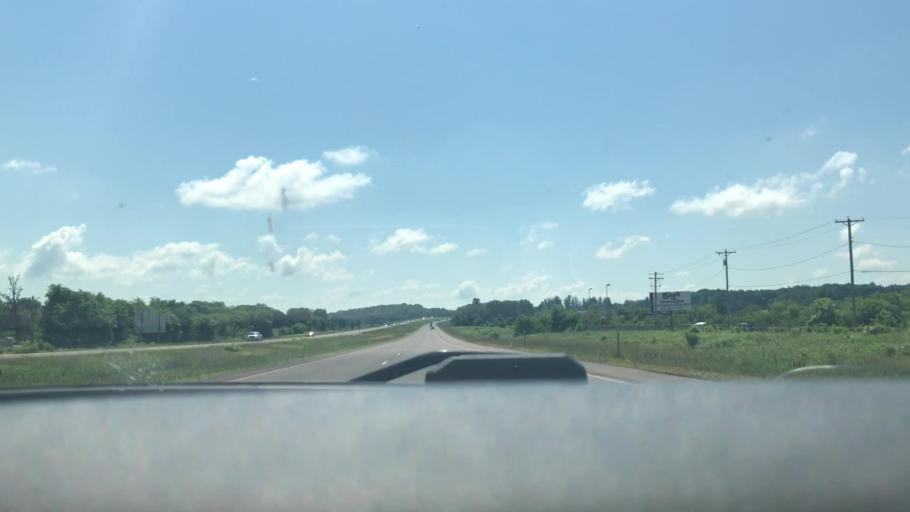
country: US
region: Wisconsin
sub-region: Chippewa County
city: Bloomer
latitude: 45.0966
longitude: -91.5000
